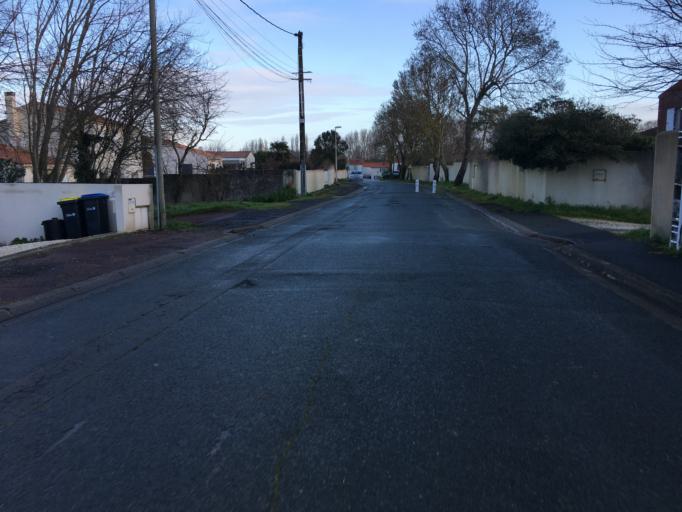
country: FR
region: Poitou-Charentes
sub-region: Departement de la Charente-Maritime
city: Nieul-sur-Mer
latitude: 46.2043
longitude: -1.1654
